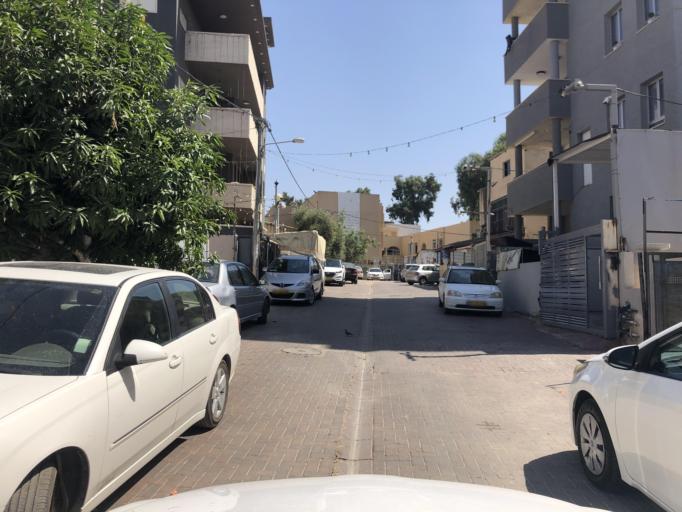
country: IL
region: Central District
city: Jaljulya
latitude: 32.1544
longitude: 34.9545
